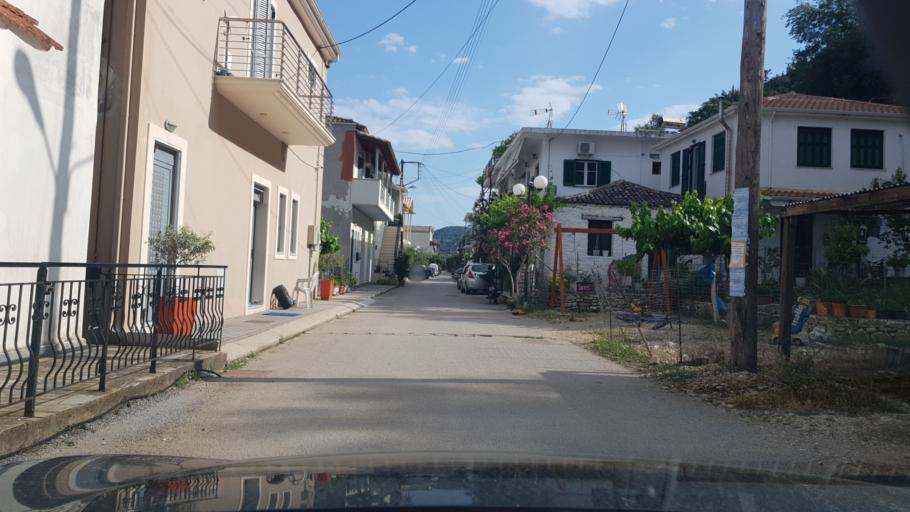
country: GR
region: Ionian Islands
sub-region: Lefkada
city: Nidri
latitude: 38.6876
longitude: 20.6983
